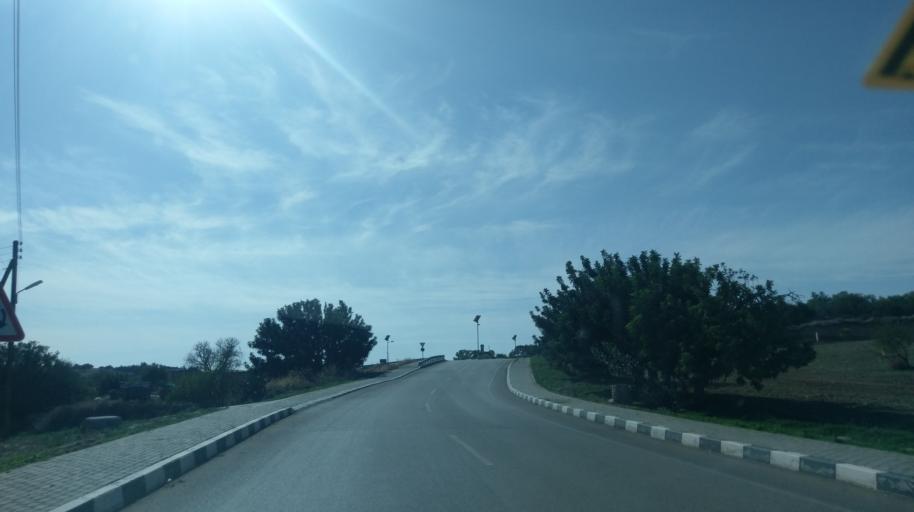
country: CY
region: Ammochostos
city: Trikomo
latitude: 35.4061
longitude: 33.9927
